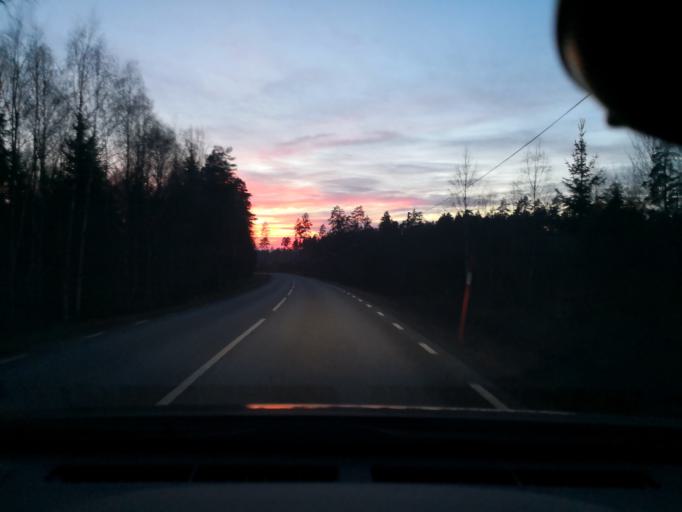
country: SE
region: OErebro
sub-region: Lindesbergs Kommun
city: Frovi
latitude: 59.3631
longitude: 15.4134
